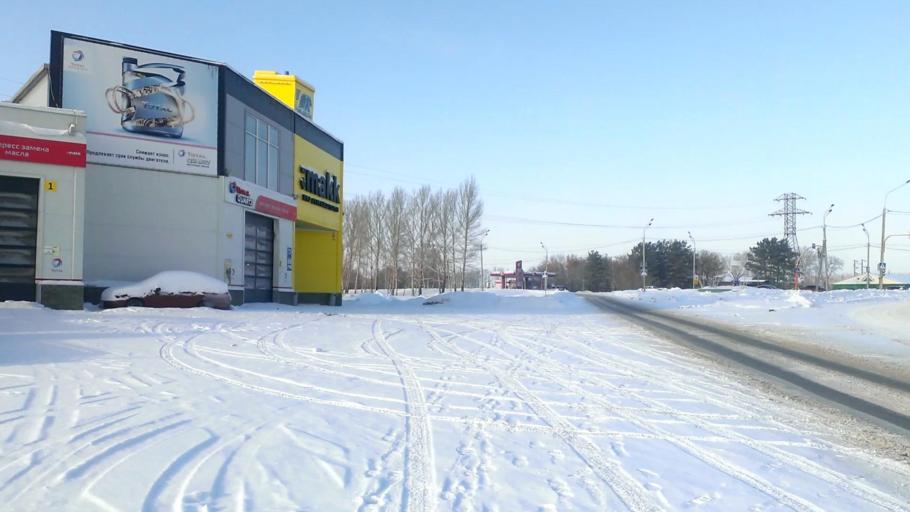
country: RU
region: Altai Krai
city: Novosilikatnyy
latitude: 53.3472
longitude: 83.6314
